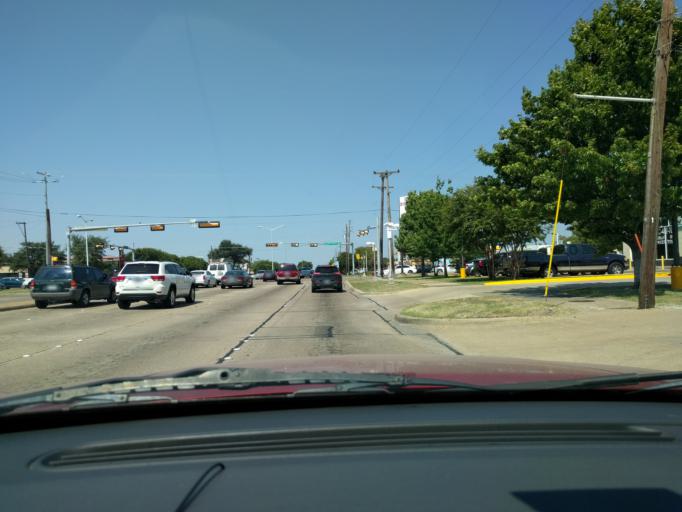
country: US
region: Texas
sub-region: Dallas County
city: Richardson
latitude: 32.9307
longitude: -96.7000
